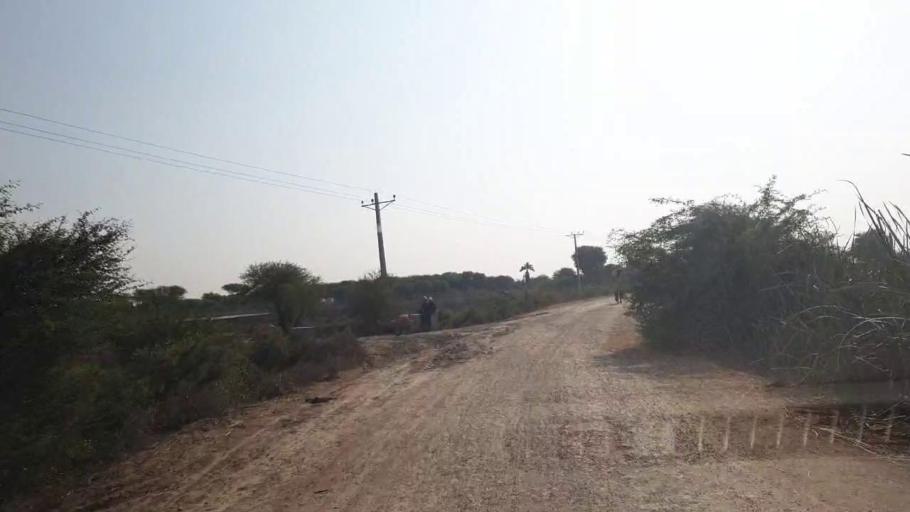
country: PK
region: Sindh
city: Kario
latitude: 24.9154
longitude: 68.6521
